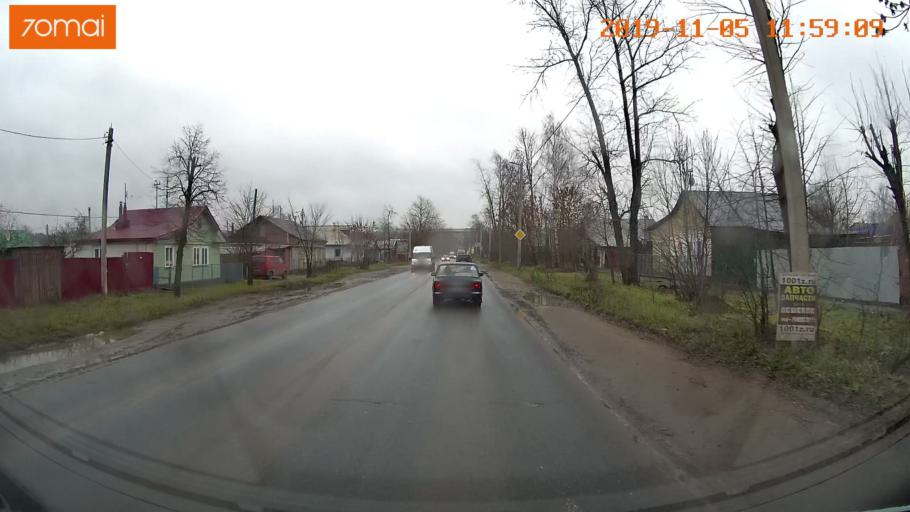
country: RU
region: Ivanovo
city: Kokhma
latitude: 56.9791
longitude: 41.0457
